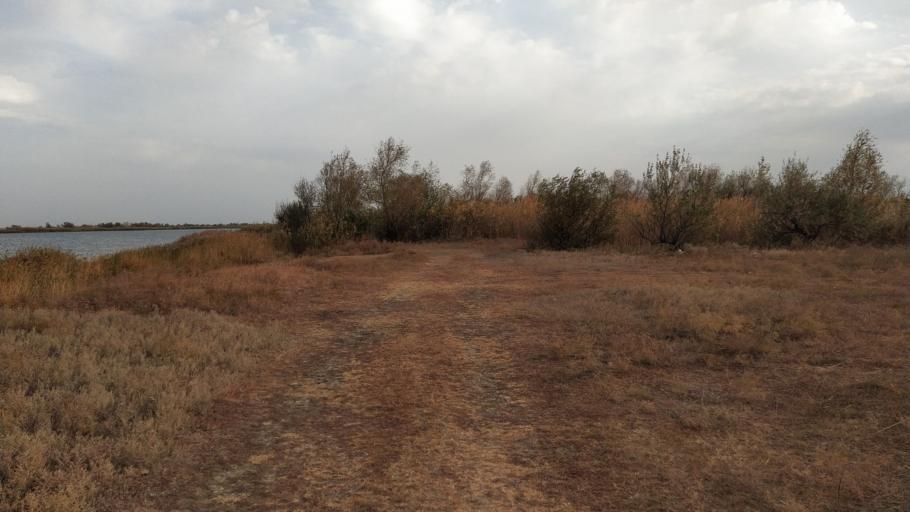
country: RU
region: Rostov
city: Kuleshovka
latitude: 47.1404
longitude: 39.5824
